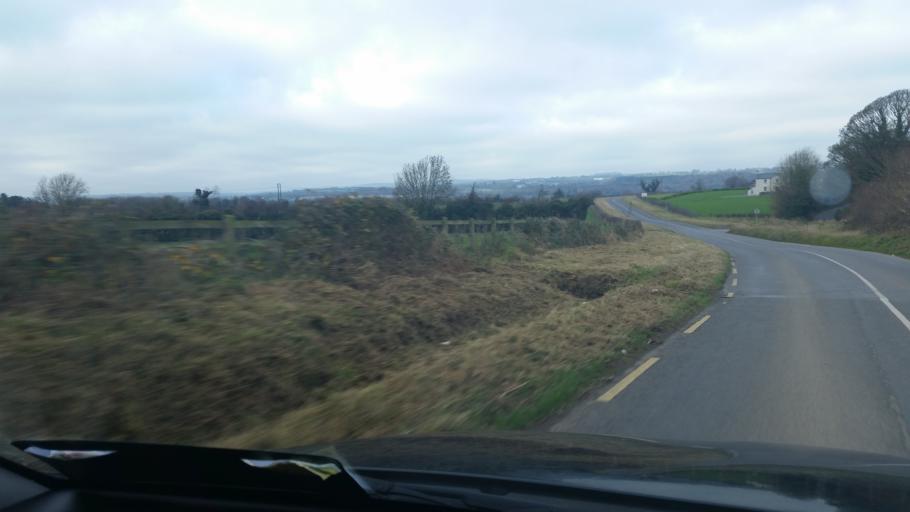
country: IE
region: Leinster
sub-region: Lu
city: Tullyallen
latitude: 53.7085
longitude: -6.4100
